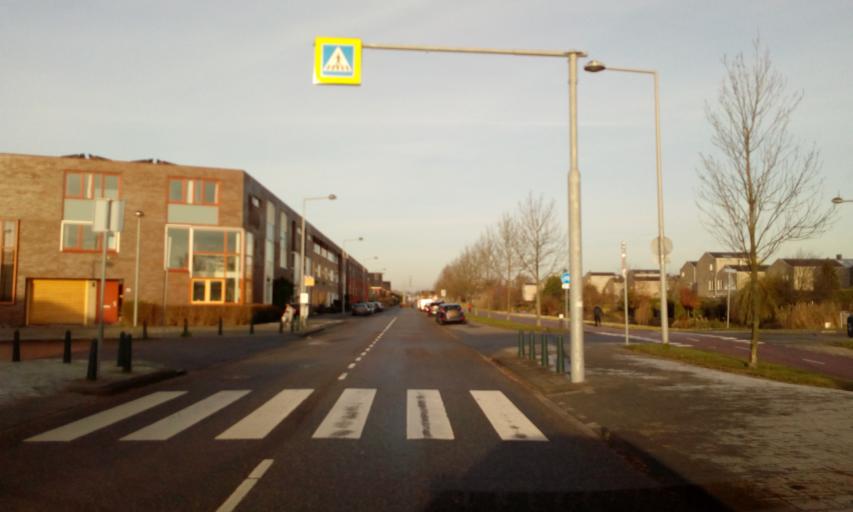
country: NL
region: South Holland
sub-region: Gemeente Den Haag
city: Ypenburg
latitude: 52.0655
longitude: 4.4108
